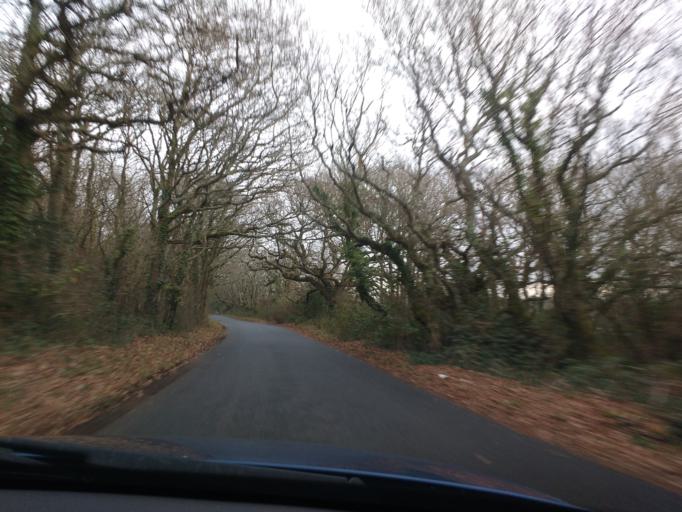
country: GB
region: England
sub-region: Isle of Wight
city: Shalfleet
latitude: 50.7100
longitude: -1.3895
